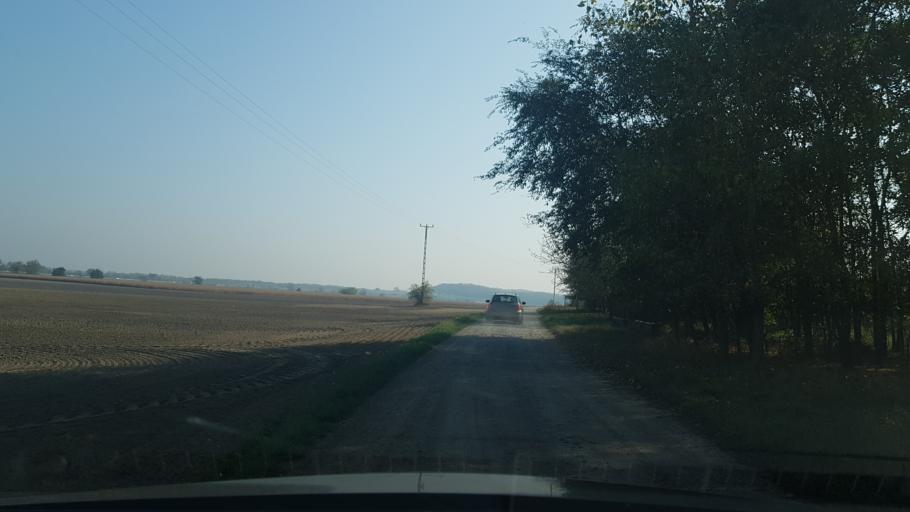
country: HU
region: Fejer
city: Adony
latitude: 47.0814
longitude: 18.8548
